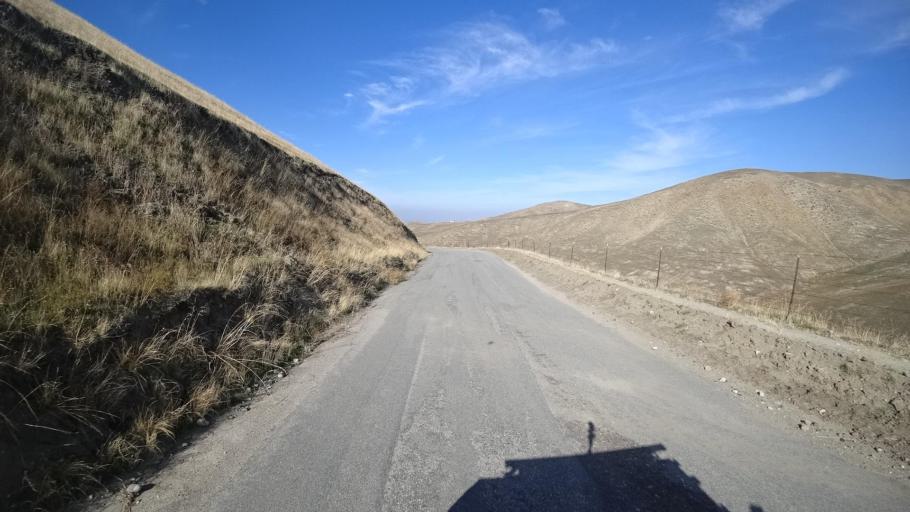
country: US
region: California
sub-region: Kern County
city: Lamont
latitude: 35.4005
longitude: -118.7816
